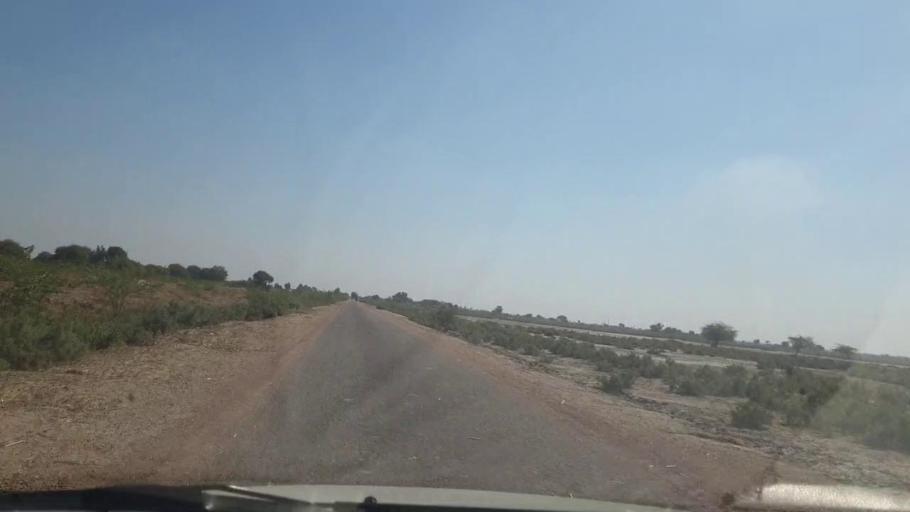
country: PK
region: Sindh
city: Mirpur Khas
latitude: 25.4935
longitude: 69.1660
